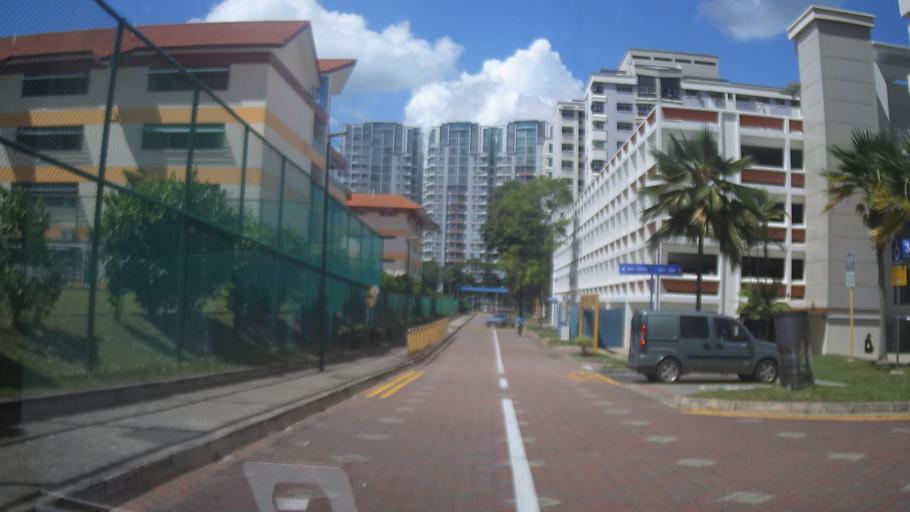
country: MY
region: Johor
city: Johor Bahru
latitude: 1.4336
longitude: 103.7851
